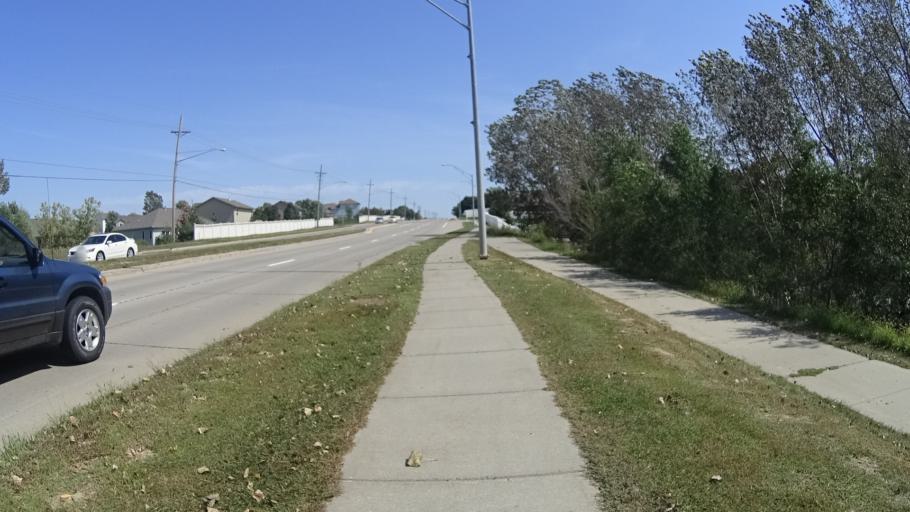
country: US
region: Nebraska
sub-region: Sarpy County
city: Papillion
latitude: 41.1761
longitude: -96.0716
